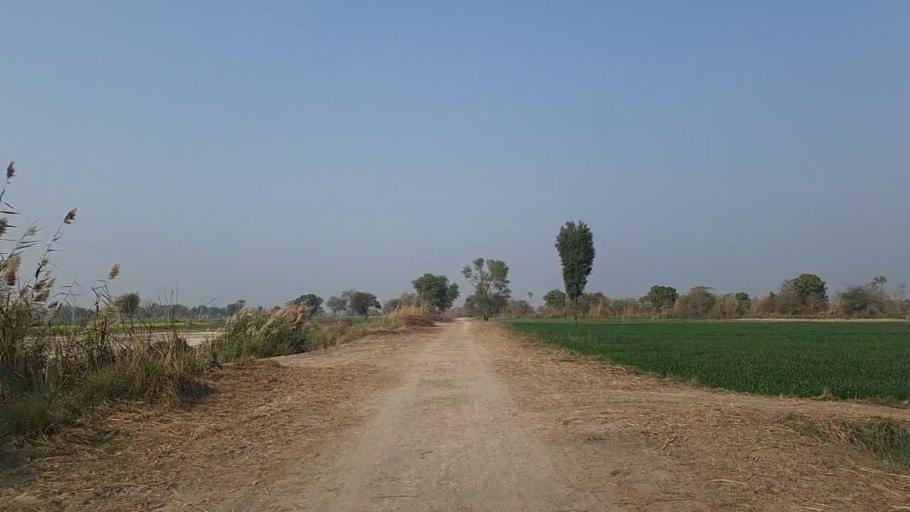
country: PK
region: Sindh
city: Nawabshah
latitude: 26.3522
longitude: 68.4741
